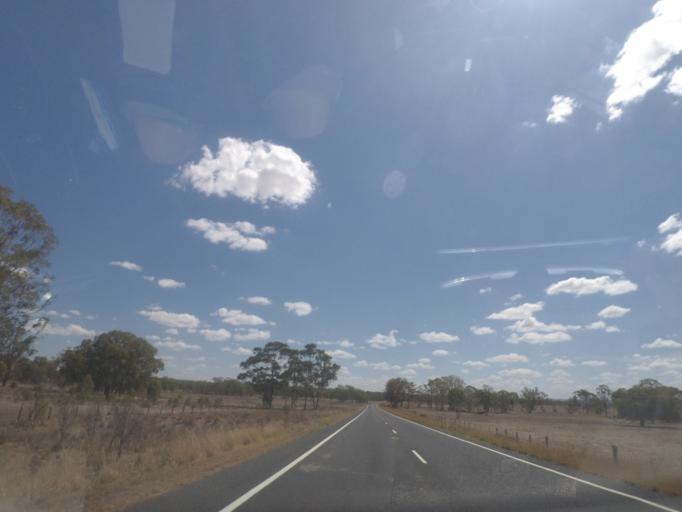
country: AU
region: Queensland
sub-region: Southern Downs
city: Warwick
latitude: -28.1813
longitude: 151.8205
